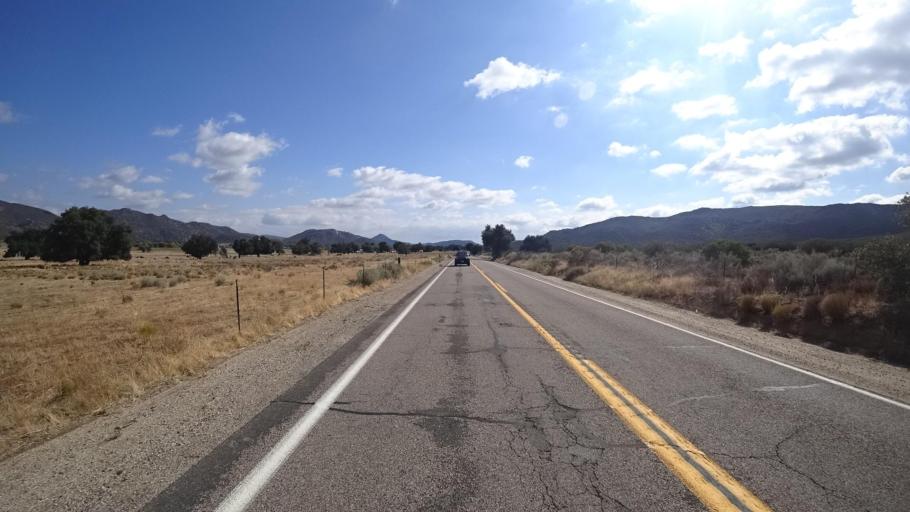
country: US
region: California
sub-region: San Diego County
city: Pine Valley
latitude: 32.7540
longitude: -116.4935
